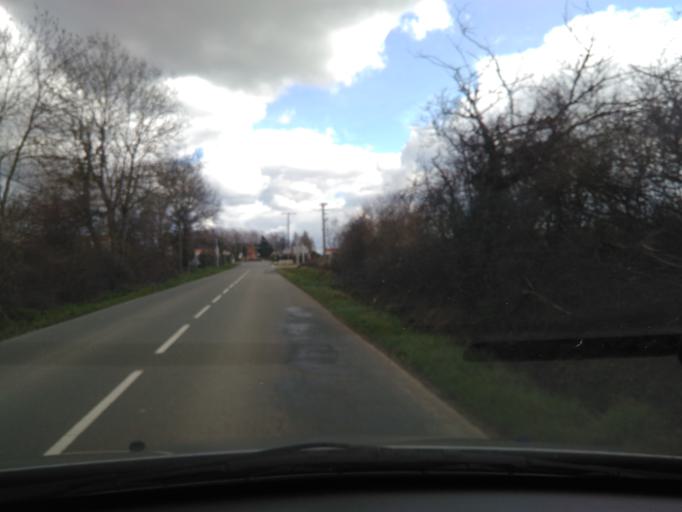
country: FR
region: Pays de la Loire
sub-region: Departement de la Vendee
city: Saint-Martin-des-Noyers
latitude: 46.6921
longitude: -1.1334
